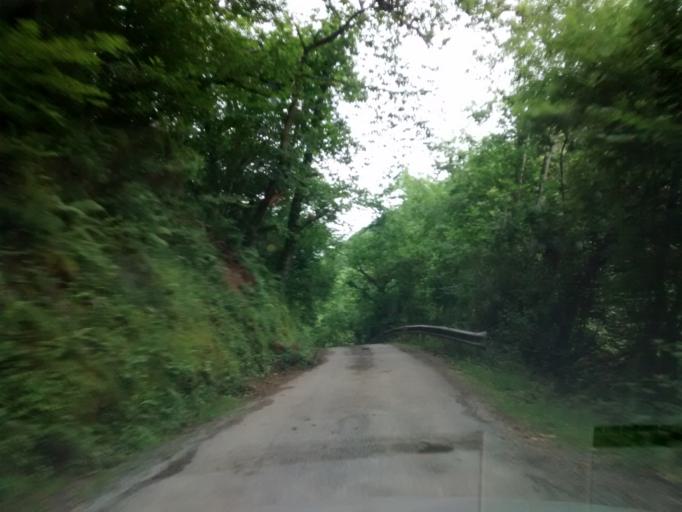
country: ES
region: Asturias
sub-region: Province of Asturias
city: Pilona
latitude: 43.2719
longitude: -5.3449
